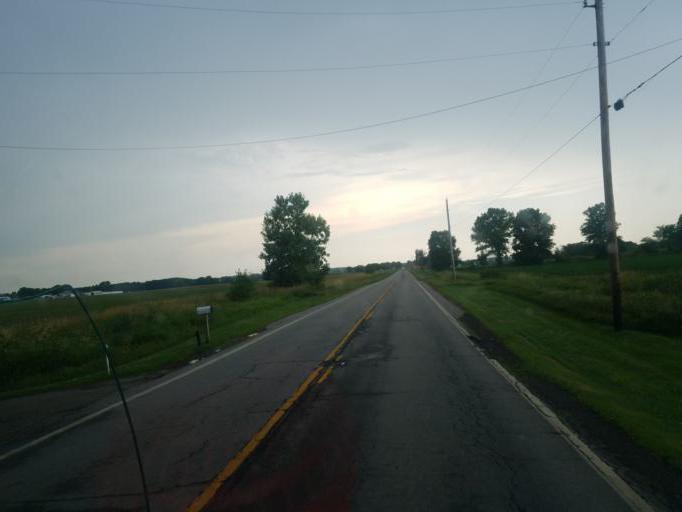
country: US
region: Ohio
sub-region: Wayne County
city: Rittman
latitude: 40.9458
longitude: -81.8024
